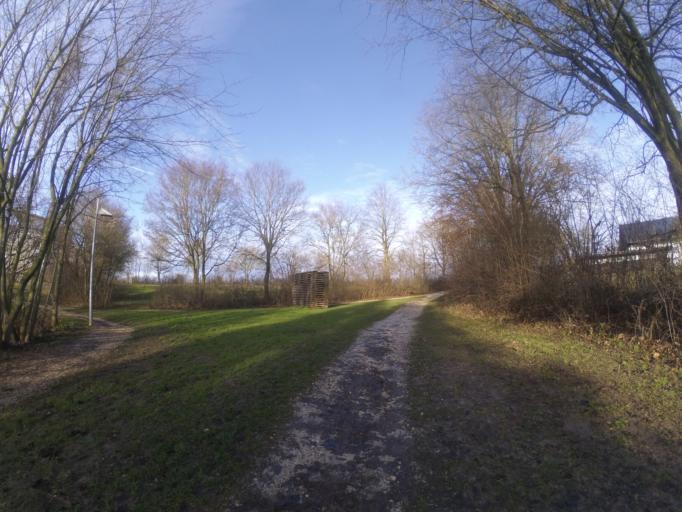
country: DE
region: Baden-Wuerttemberg
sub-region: Tuebingen Region
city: Ulm
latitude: 48.4157
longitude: 9.9469
